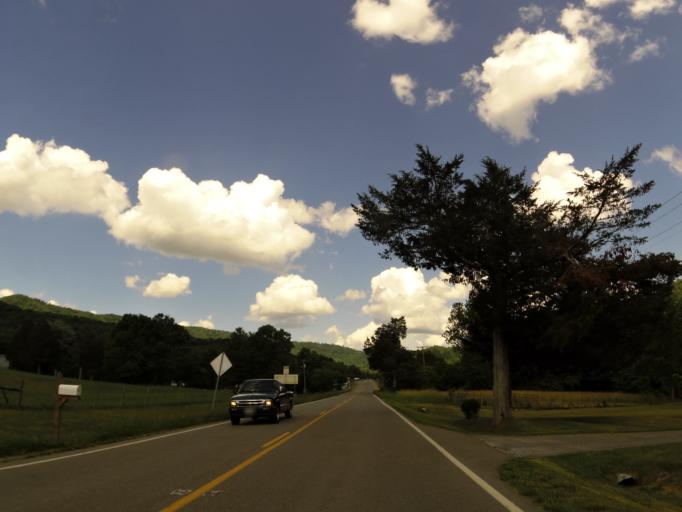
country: US
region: Virginia
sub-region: Lee County
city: Dryden
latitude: 36.7081
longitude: -82.9666
